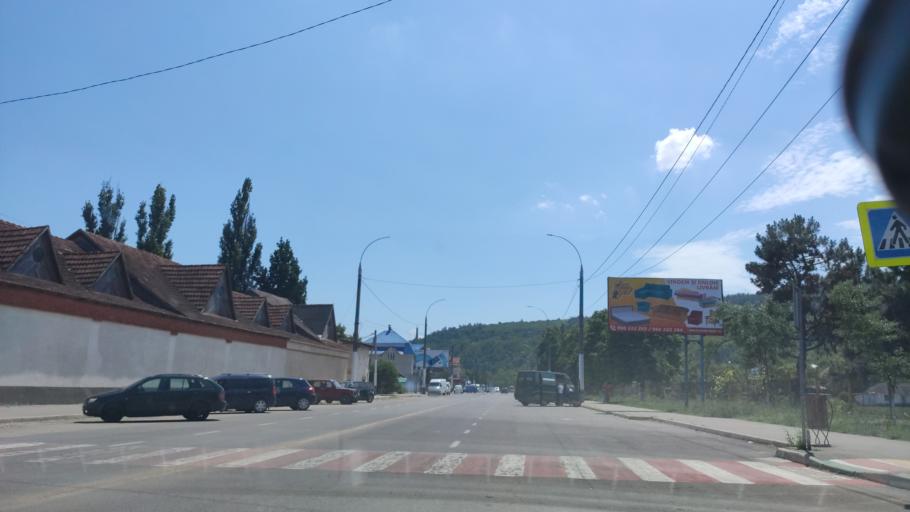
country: MD
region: Raionul Soroca
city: Soroca
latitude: 48.1490
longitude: 28.3020
